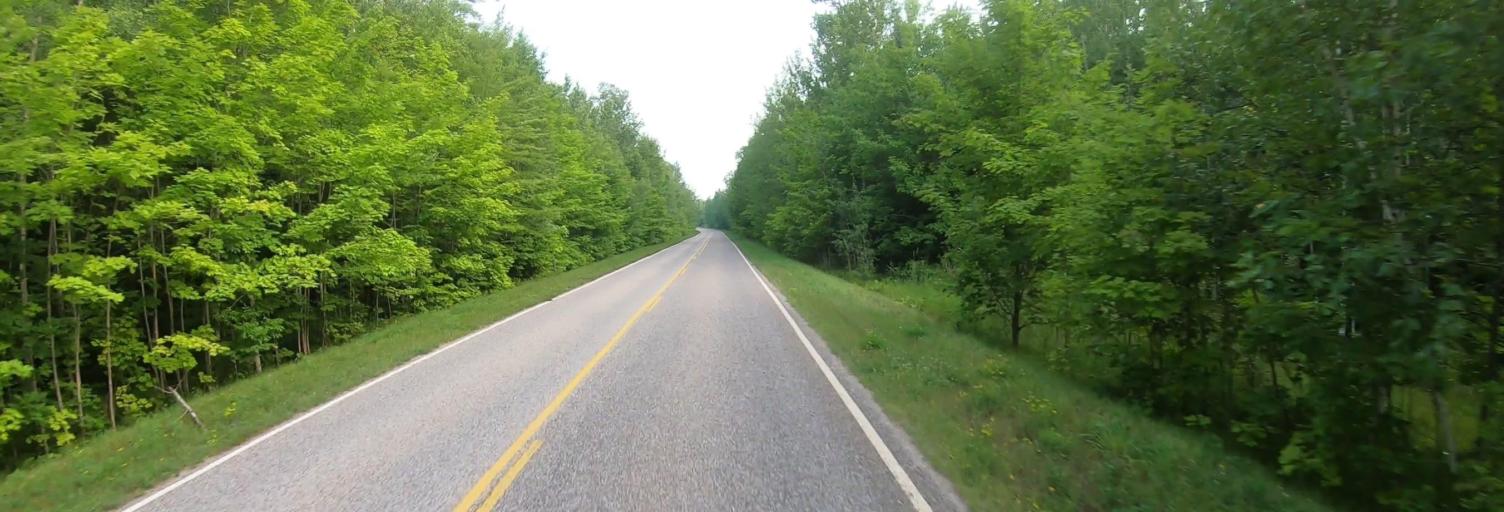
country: US
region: Michigan
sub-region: Chippewa County
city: Sault Ste. Marie
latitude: 46.4556
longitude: -84.8547
